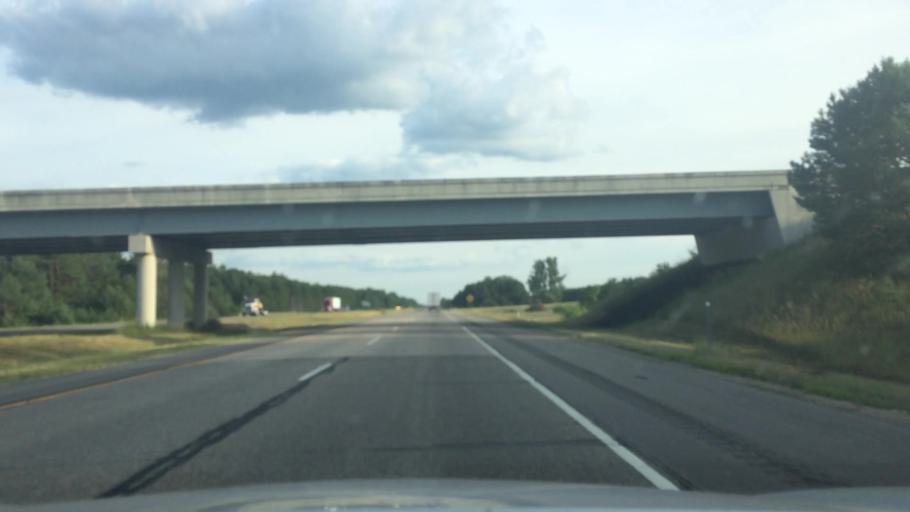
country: US
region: Wisconsin
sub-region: Portage County
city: Plover
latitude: 44.2595
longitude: -89.5241
